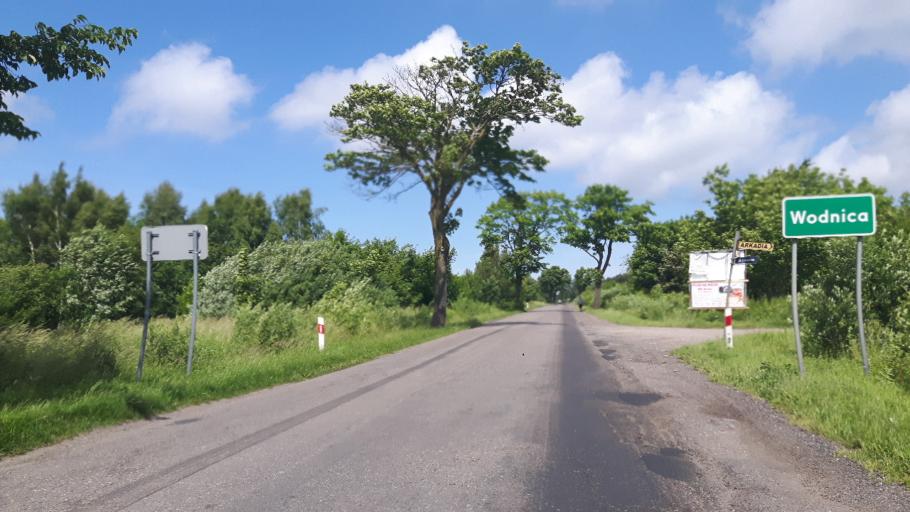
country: PL
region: Pomeranian Voivodeship
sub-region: Powiat slupski
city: Ustka
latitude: 54.5602
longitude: 16.8442
